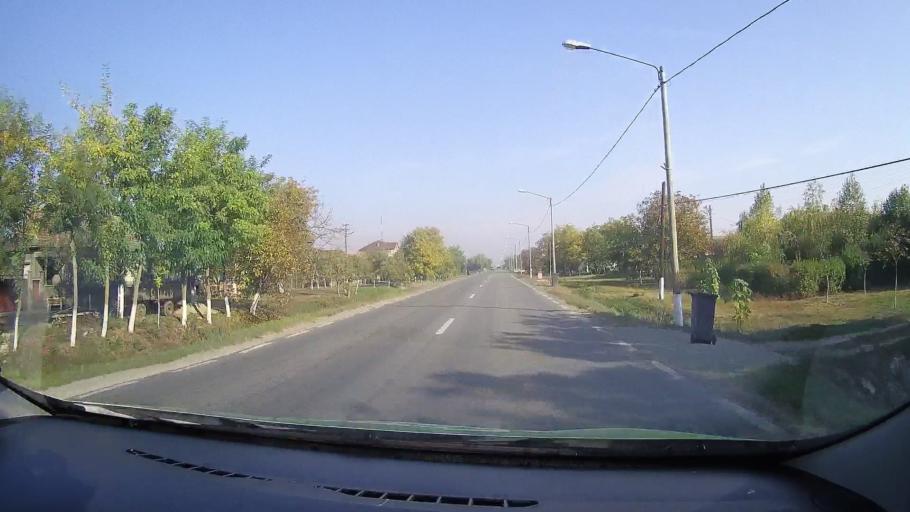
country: RO
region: Arad
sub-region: Comuna Pilu
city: Pilu
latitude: 46.5773
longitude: 21.3429
